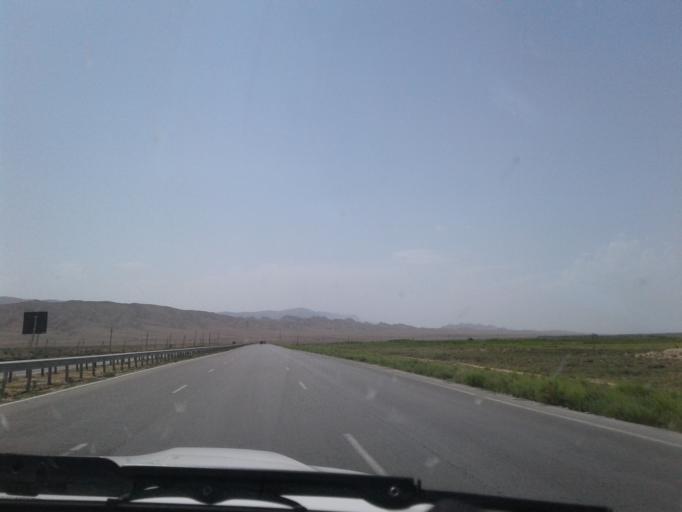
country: IR
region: Razavi Khorasan
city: Dargaz
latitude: 37.5923
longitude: 59.2327
